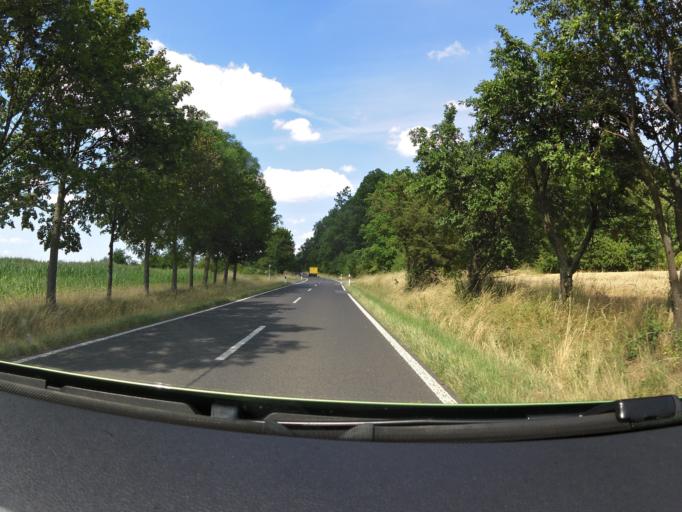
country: DE
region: Thuringia
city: Horselgau
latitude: 50.9595
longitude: 10.5978
